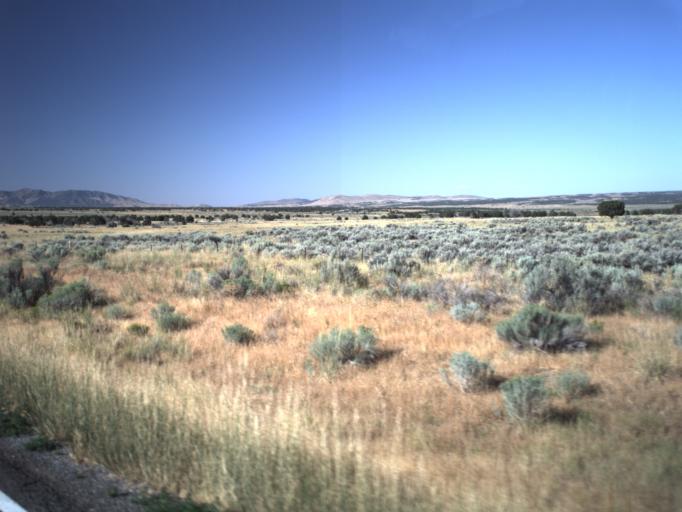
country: US
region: Utah
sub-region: Juab County
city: Mona
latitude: 39.8644
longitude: -112.1381
